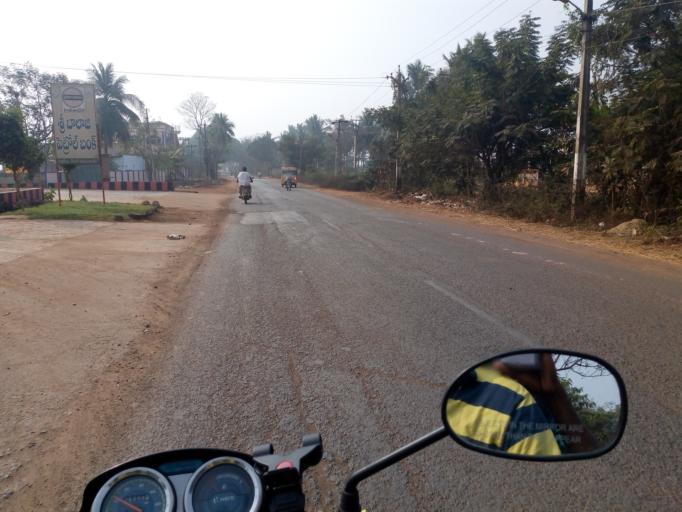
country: IN
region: Andhra Pradesh
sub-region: West Godavari
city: Tadepallegudem
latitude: 16.8142
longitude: 81.4083
